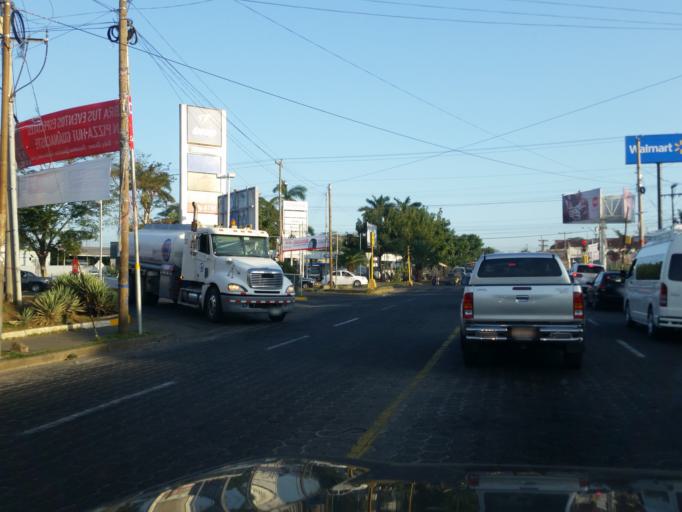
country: NI
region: Managua
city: Managua
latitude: 12.1418
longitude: -86.2956
